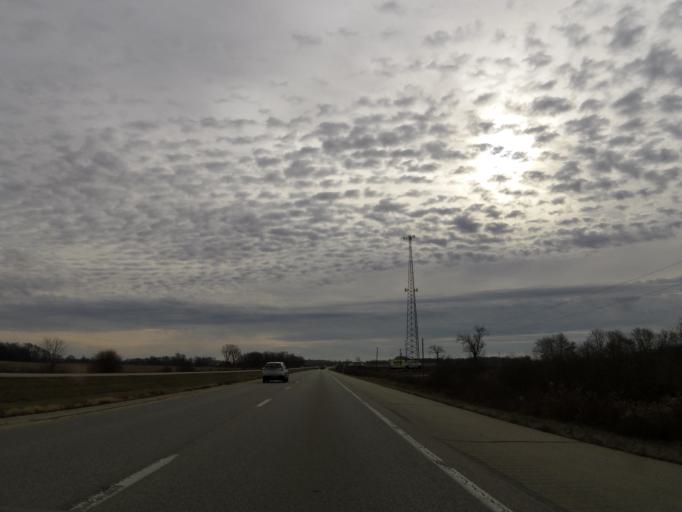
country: US
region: Indiana
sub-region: Hendricks County
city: Pittsboro
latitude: 39.9194
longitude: -86.5784
